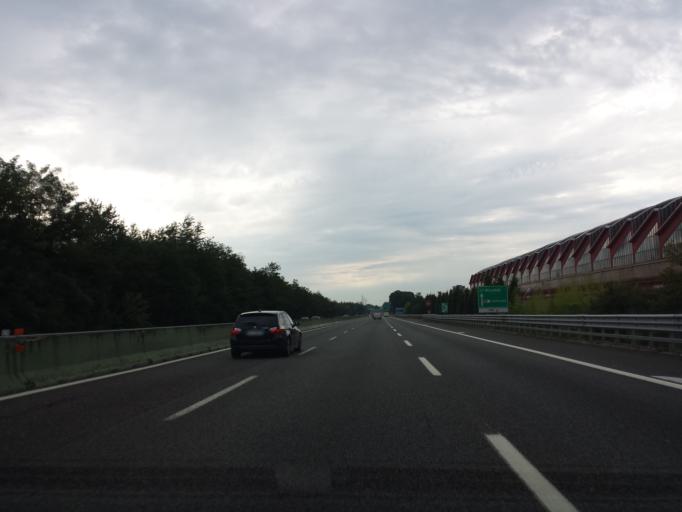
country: IT
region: Lombardy
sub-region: Provincia di Varese
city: Marnate
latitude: 45.6148
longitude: 8.9170
